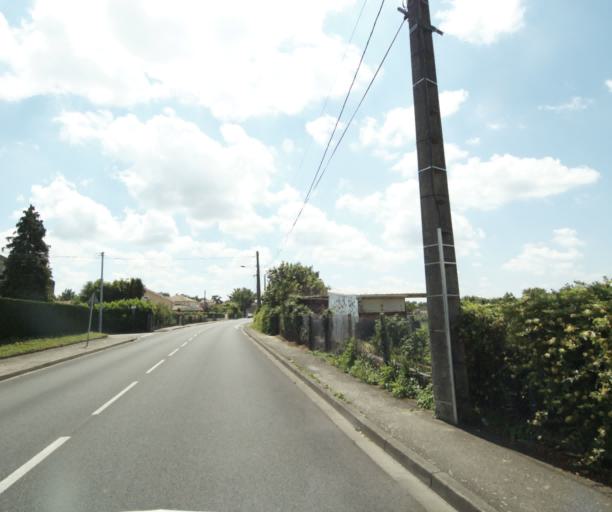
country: FR
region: Midi-Pyrenees
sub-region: Departement du Tarn-et-Garonne
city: Montauban
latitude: 44.0337
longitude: 1.3536
